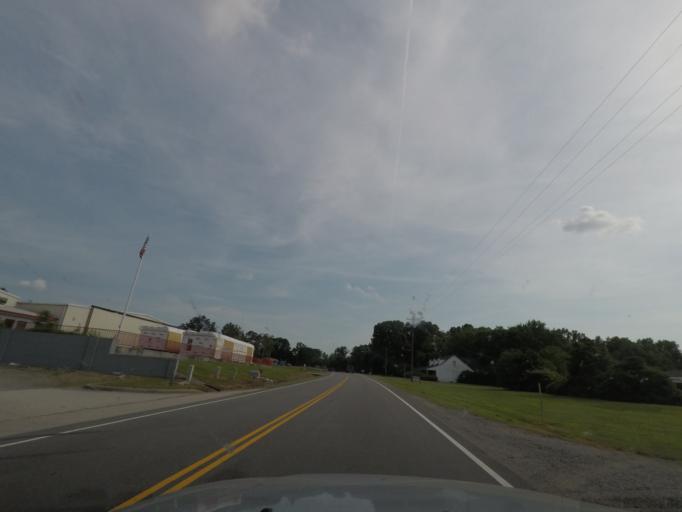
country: US
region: Virginia
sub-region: Mecklenburg County
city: Chase City
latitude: 36.8606
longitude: -78.5888
